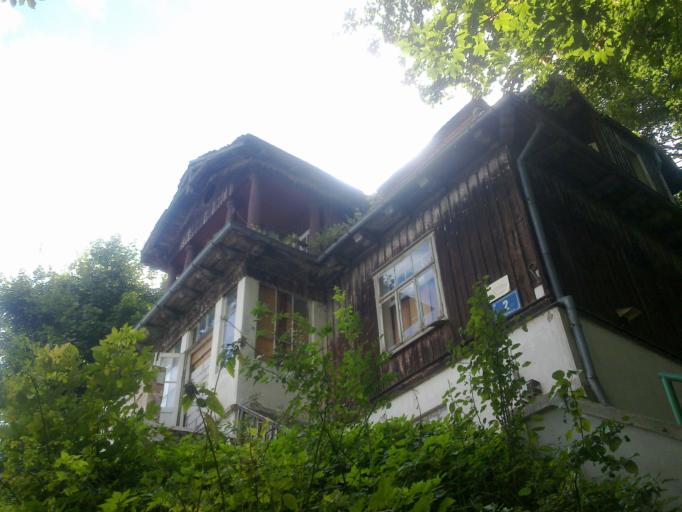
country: PL
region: Pomeranian Voivodeship
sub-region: Gdynia
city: Gdynia
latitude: 54.5153
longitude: 18.5452
